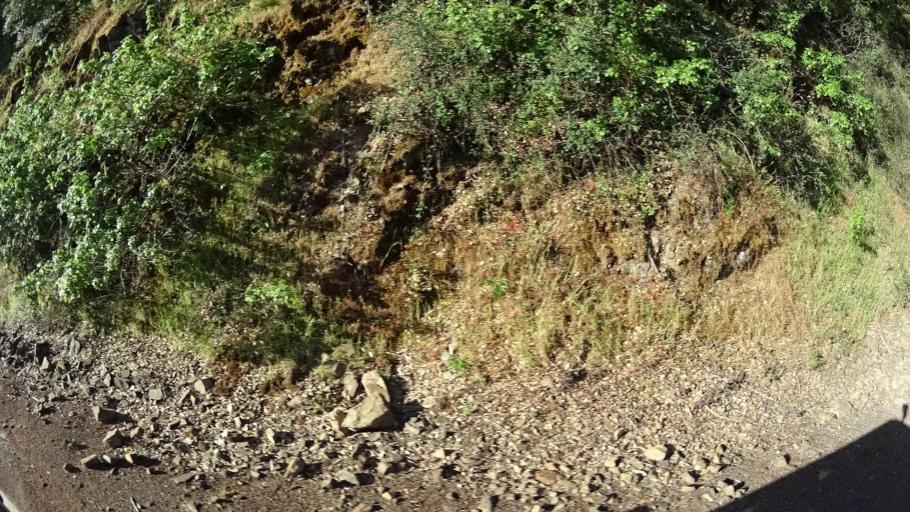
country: US
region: California
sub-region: Lake County
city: North Lakeport
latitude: 39.0925
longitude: -122.9532
